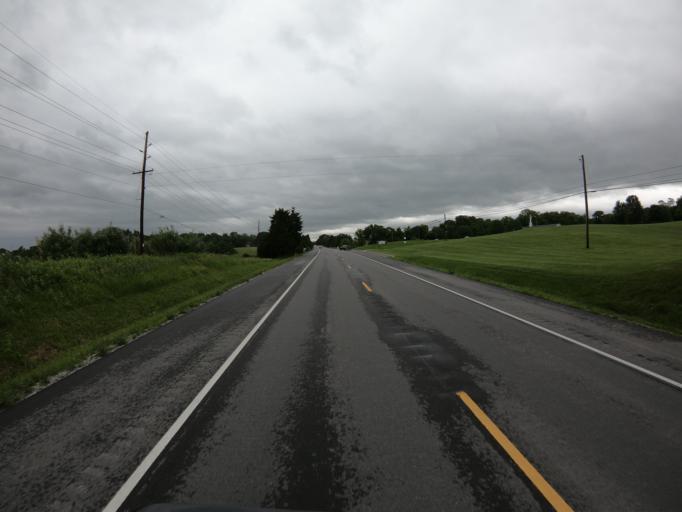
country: US
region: Maryland
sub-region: Washington County
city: Keedysville
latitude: 39.4701
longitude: -77.7148
